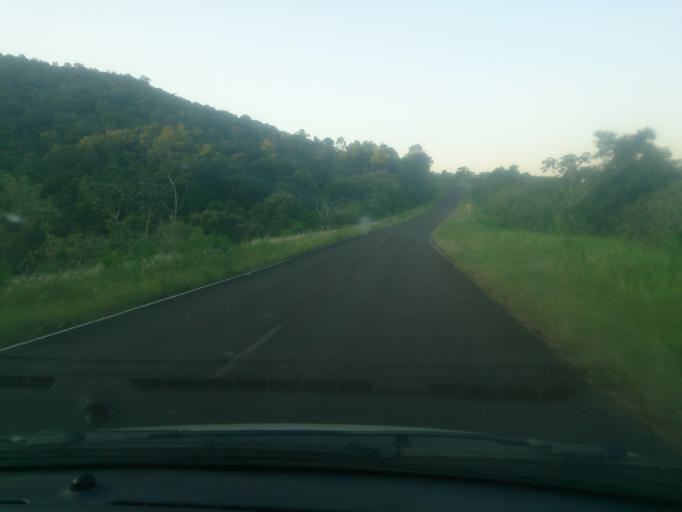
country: AR
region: Misiones
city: Panambi
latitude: -27.6538
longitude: -54.9082
